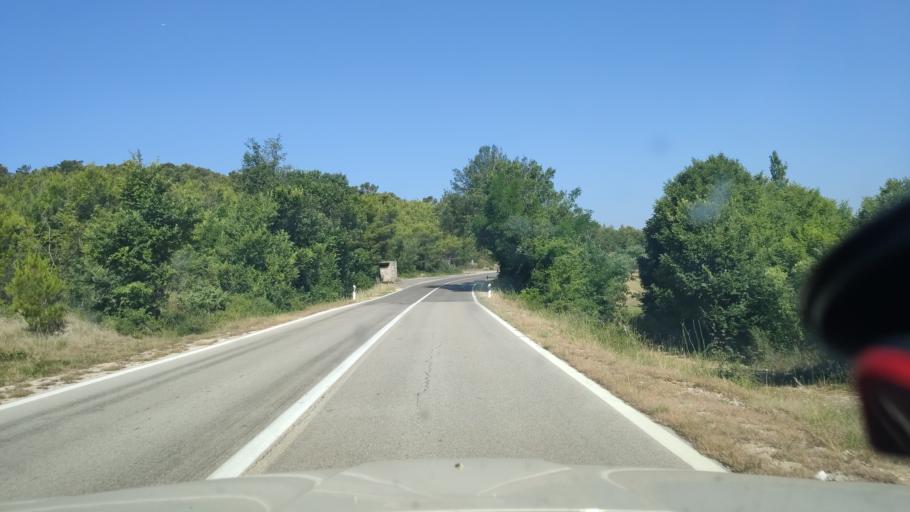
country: HR
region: Sibensko-Kniniska
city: Zaton
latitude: 43.9161
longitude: 15.8279
